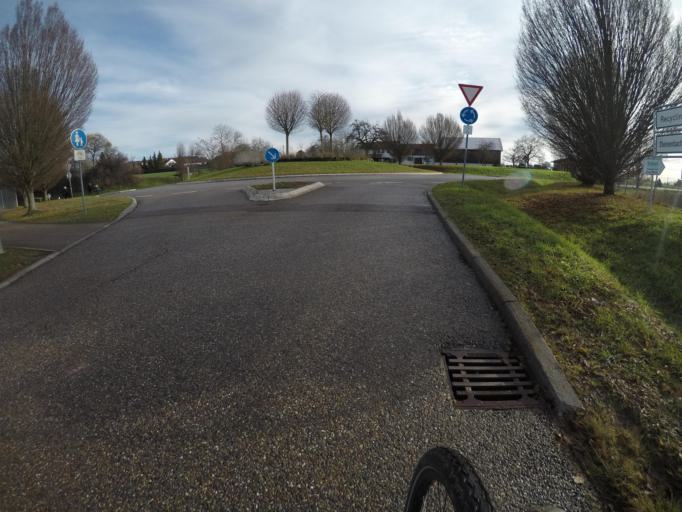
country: DE
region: Baden-Wuerttemberg
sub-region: Regierungsbezirk Stuttgart
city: Baltmannsweiler
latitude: 48.7571
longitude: 9.4457
